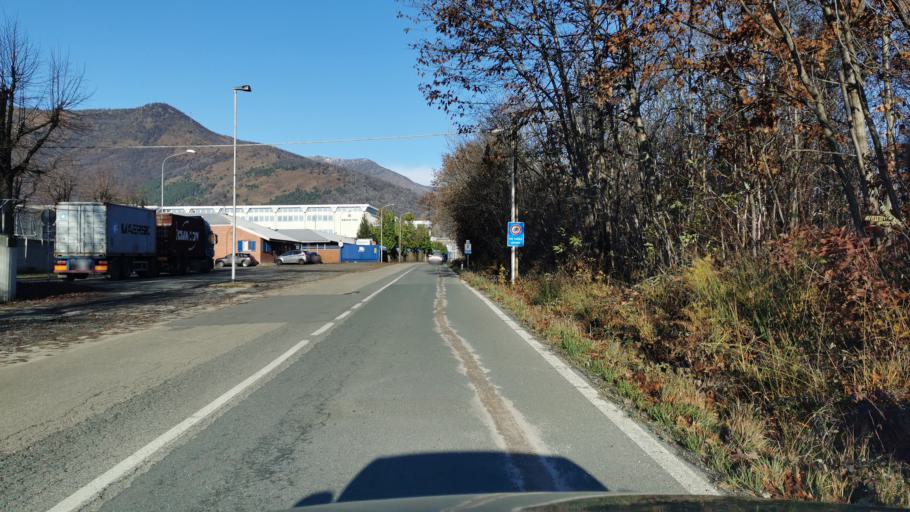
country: IT
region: Piedmont
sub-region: Provincia di Torino
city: La Cassa
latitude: 45.1690
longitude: 7.5229
